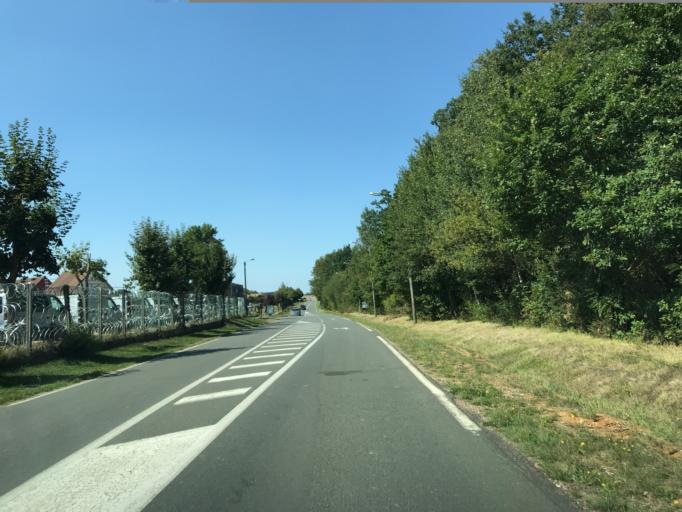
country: FR
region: Haute-Normandie
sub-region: Departement de l'Eure
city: La Chapelle-Reanville
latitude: 49.0954
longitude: 1.3904
